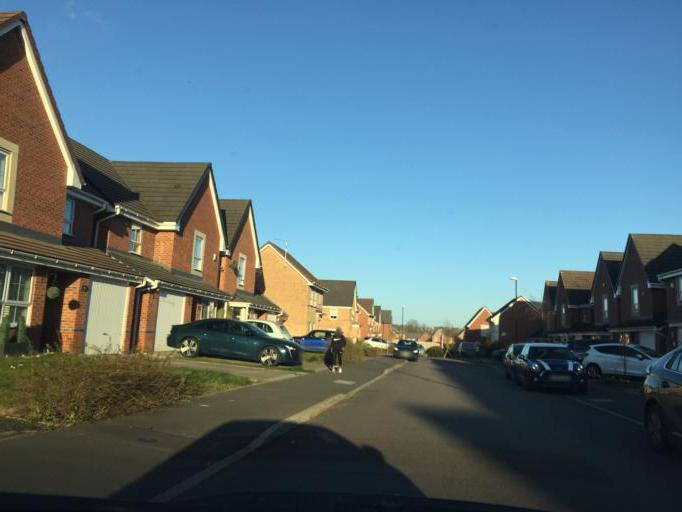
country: GB
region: England
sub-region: Coventry
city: Coventry
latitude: 52.4029
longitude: -1.4686
